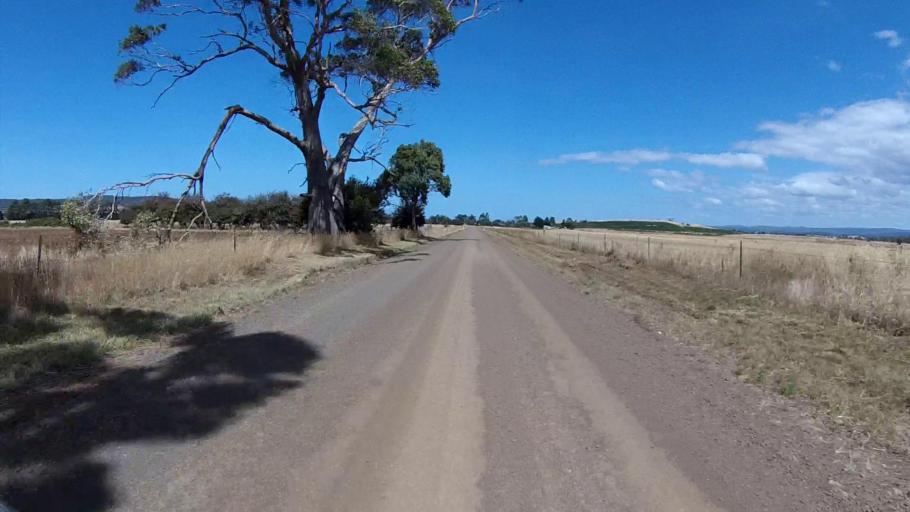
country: AU
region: Tasmania
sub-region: Break O'Day
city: St Helens
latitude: -41.9967
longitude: 148.0672
